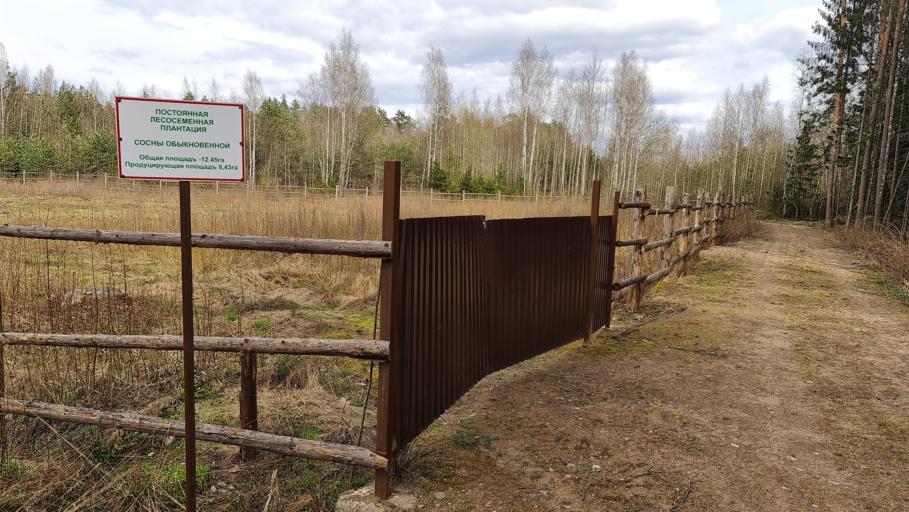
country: BY
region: Vitebsk
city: Byahoml'
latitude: 54.7494
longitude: 28.0480
